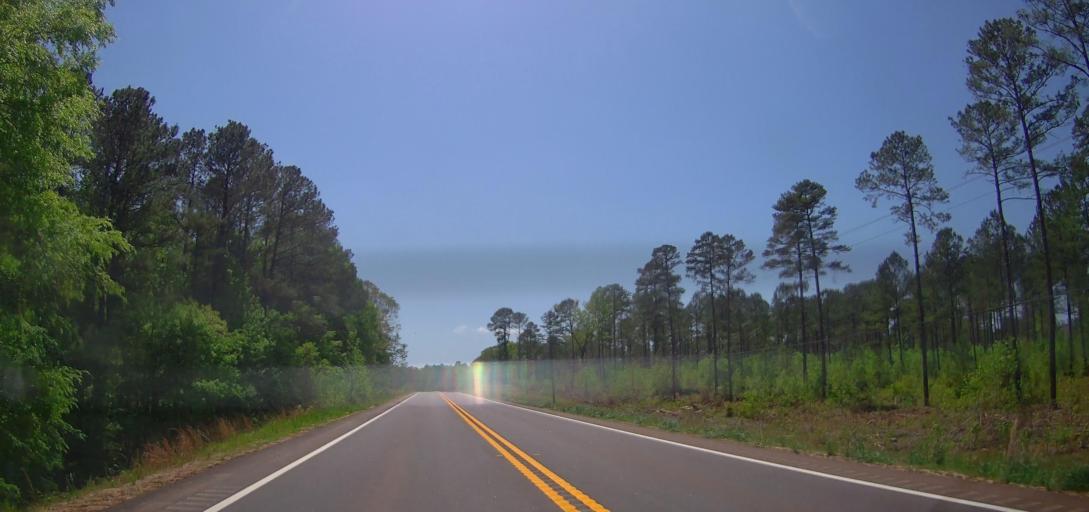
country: US
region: Georgia
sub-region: Putnam County
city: Eatonton
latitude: 33.2585
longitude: -83.4223
